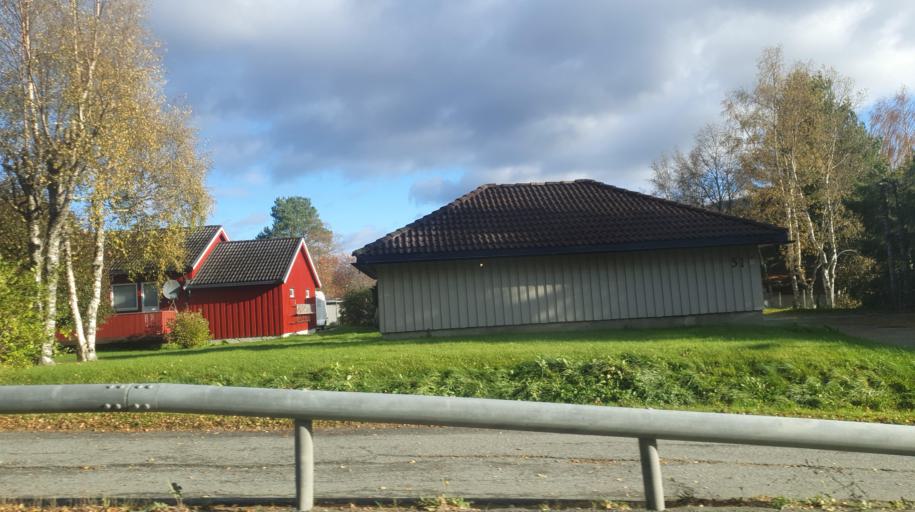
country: NO
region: Sor-Trondelag
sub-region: Klaebu
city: Klaebu
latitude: 63.2996
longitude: 10.4735
